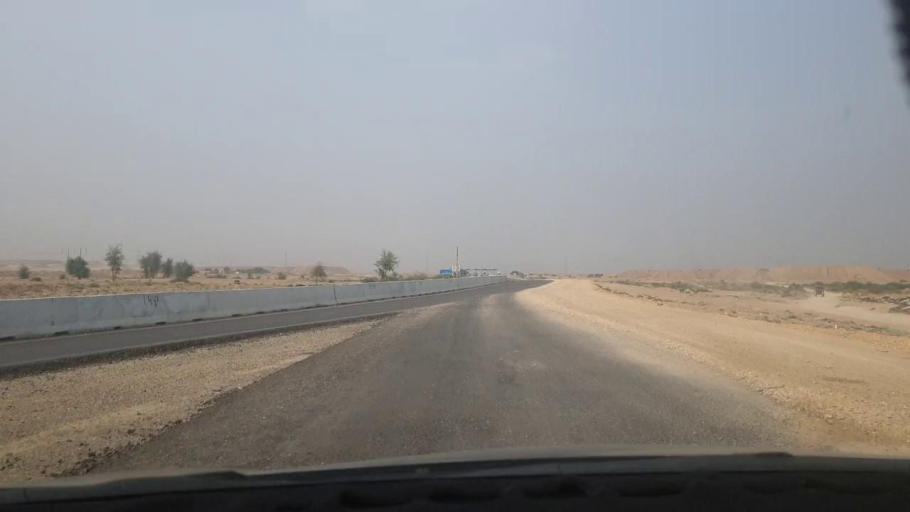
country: PK
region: Sindh
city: Matiari
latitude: 25.5733
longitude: 68.3148
